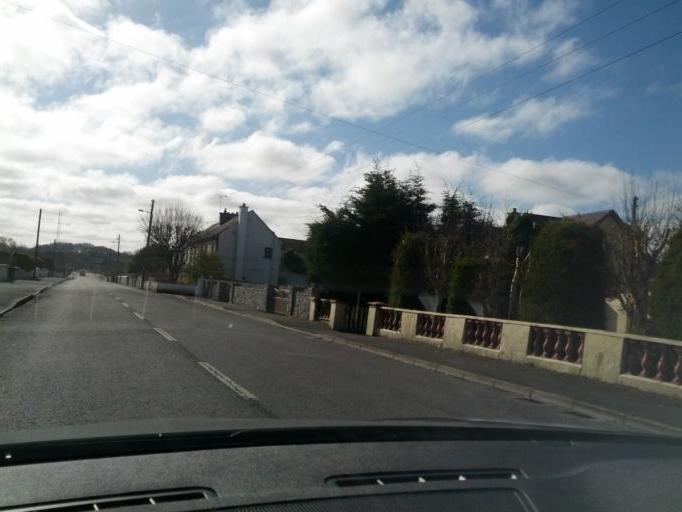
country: IE
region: Connaught
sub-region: County Galway
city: Ballinasloe
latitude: 53.3393
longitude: -8.2415
